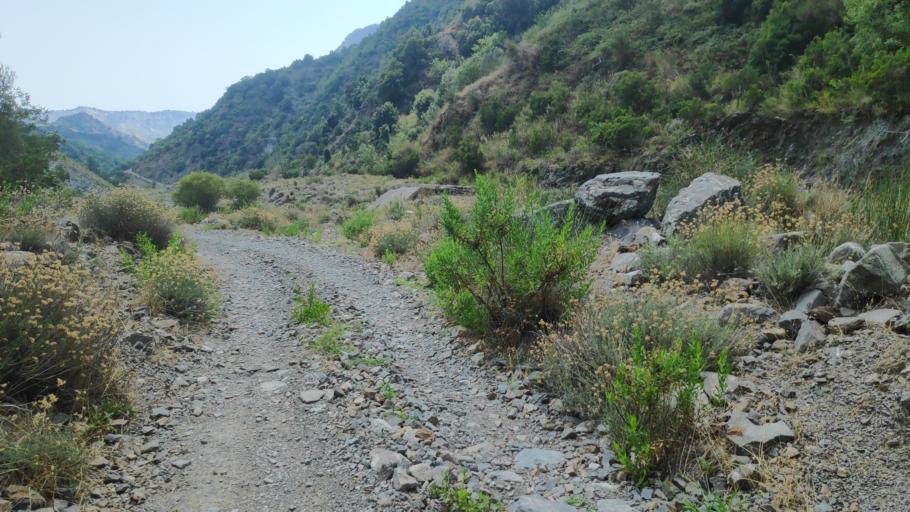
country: IT
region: Calabria
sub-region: Provincia di Reggio Calabria
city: Bivongi
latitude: 38.4947
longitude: 16.4460
